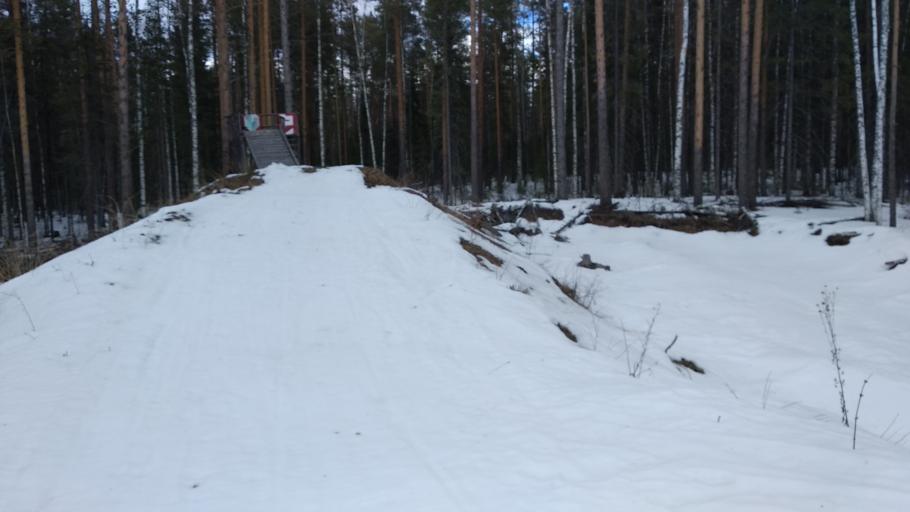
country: RU
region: Sverdlovsk
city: Karpinsk
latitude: 59.6777
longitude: 59.7907
